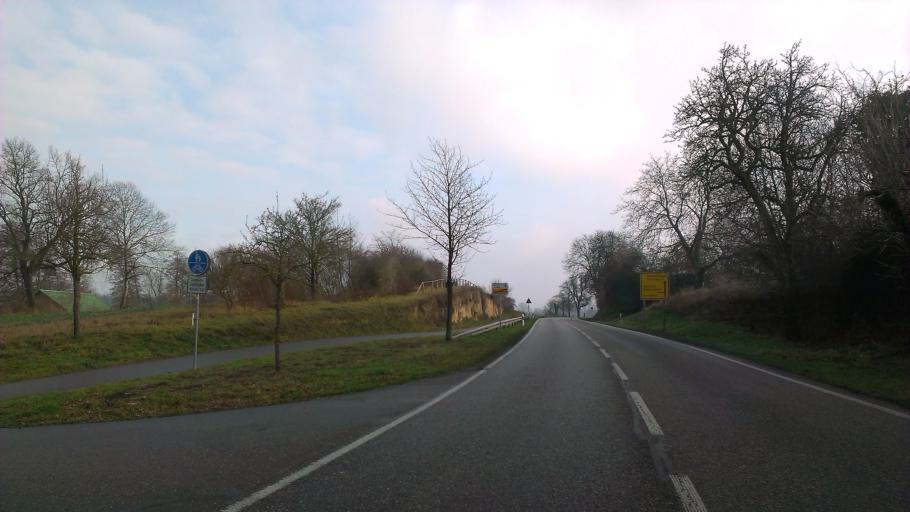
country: DE
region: Baden-Wuerttemberg
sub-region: Karlsruhe Region
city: Ubstadt-Weiher
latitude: 49.1400
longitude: 8.6747
